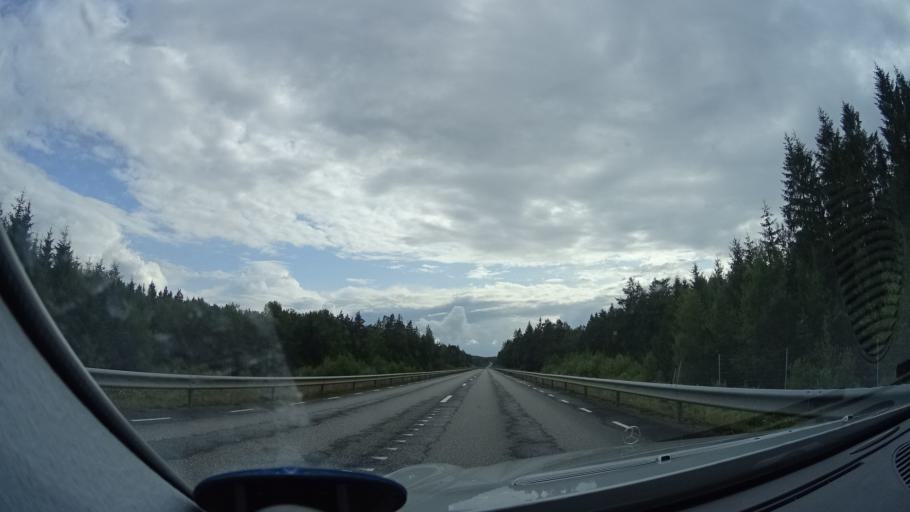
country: SE
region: Blekinge
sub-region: Karlshamns Kommun
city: Svangsta
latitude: 56.2709
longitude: 14.8552
